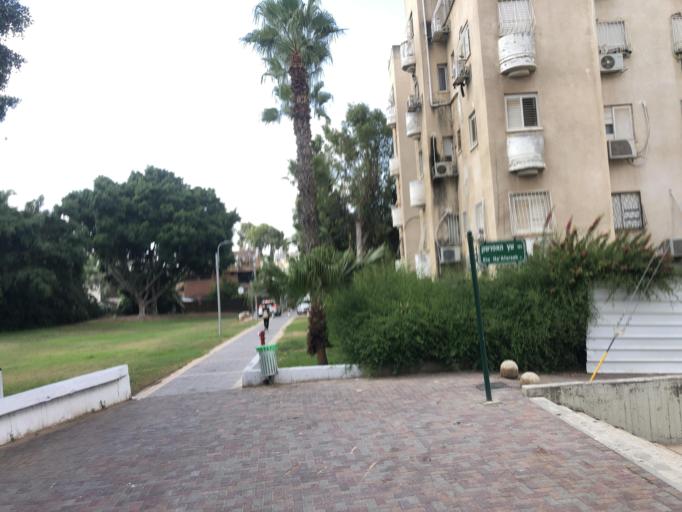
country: IL
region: Central District
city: Yehud
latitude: 32.0352
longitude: 34.8888
